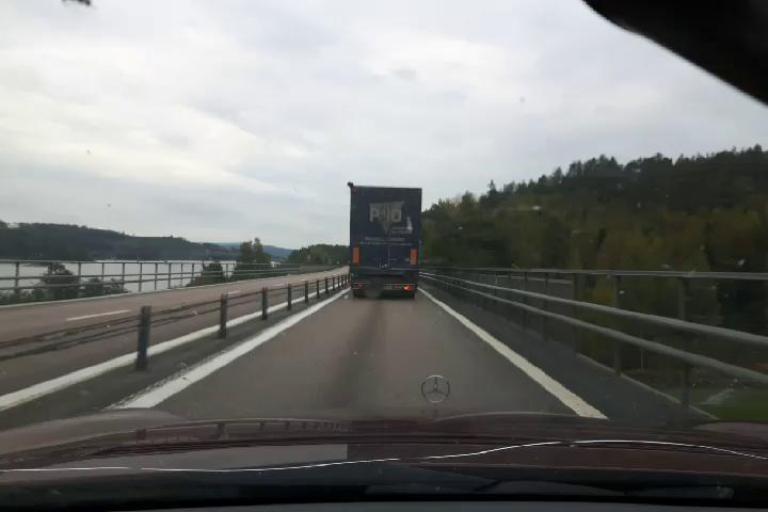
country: SE
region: Vaesternorrland
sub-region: Haernoesands Kommun
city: Haernoesand
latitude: 62.8243
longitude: 17.9697
